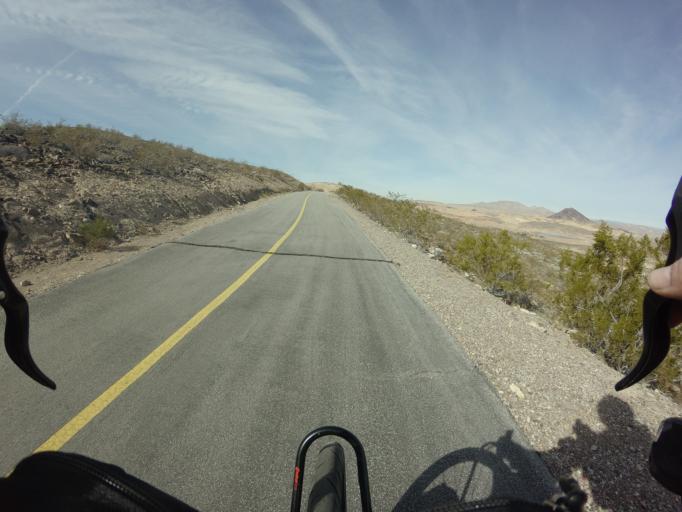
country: US
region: Nevada
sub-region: Clark County
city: Henderson
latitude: 36.1058
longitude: -114.8935
